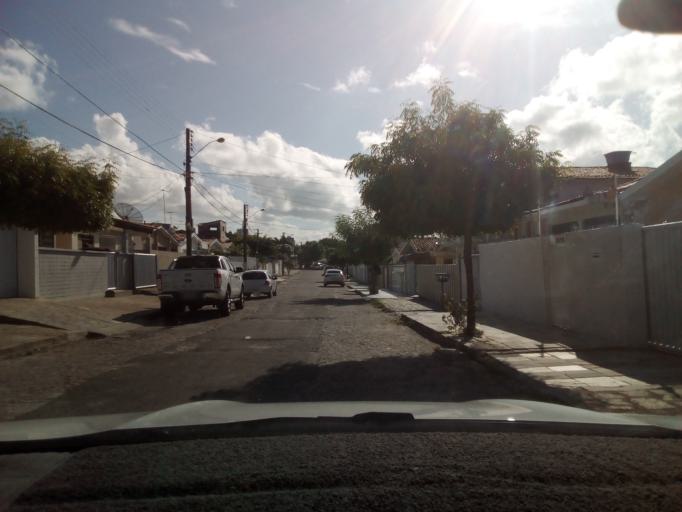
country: BR
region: Paraiba
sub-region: Joao Pessoa
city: Joao Pessoa
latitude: -7.1050
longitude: -34.8558
